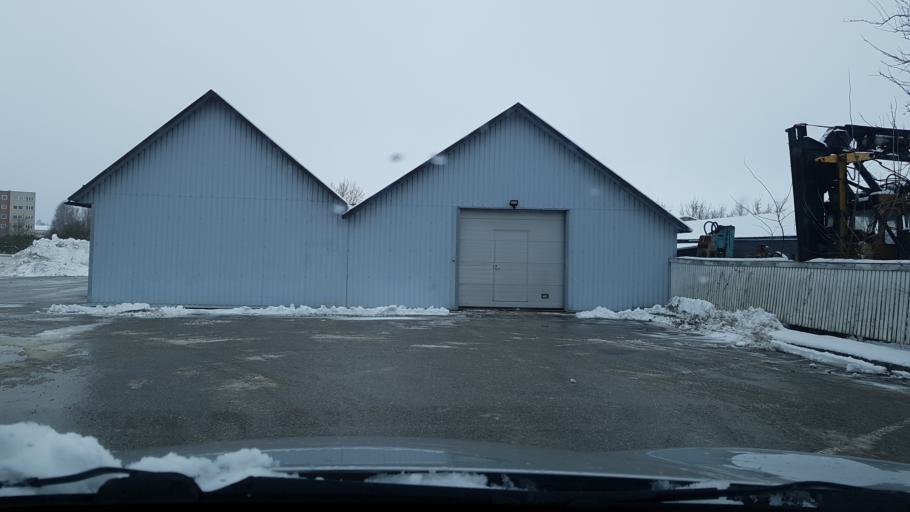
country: EE
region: Vorumaa
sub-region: Voru linn
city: Voru
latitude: 57.8436
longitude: 27.0148
